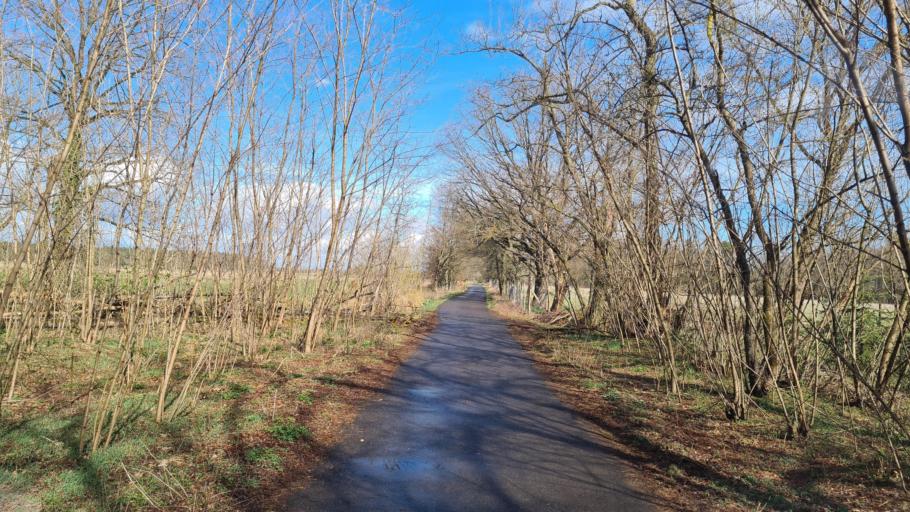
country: DE
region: Brandenburg
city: Altdobern
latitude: 51.7062
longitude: 14.0377
